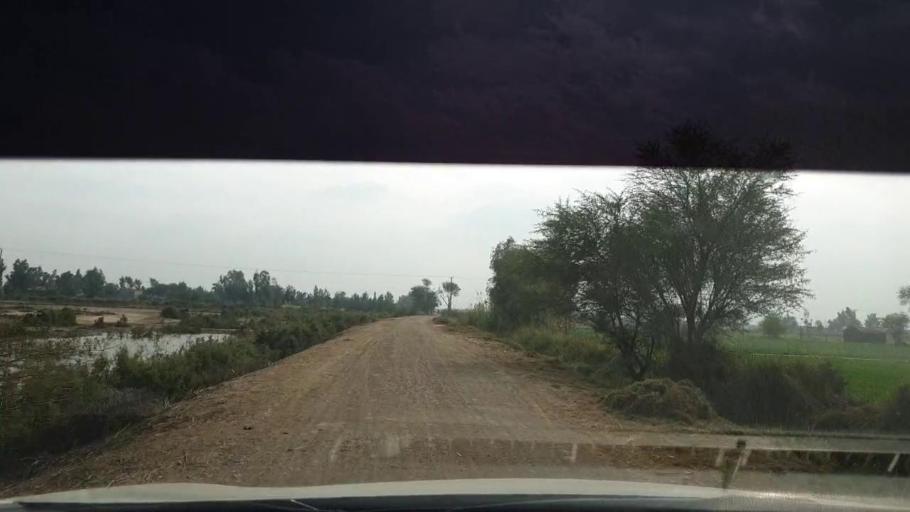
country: PK
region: Sindh
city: Berani
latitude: 25.7596
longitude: 68.8767
